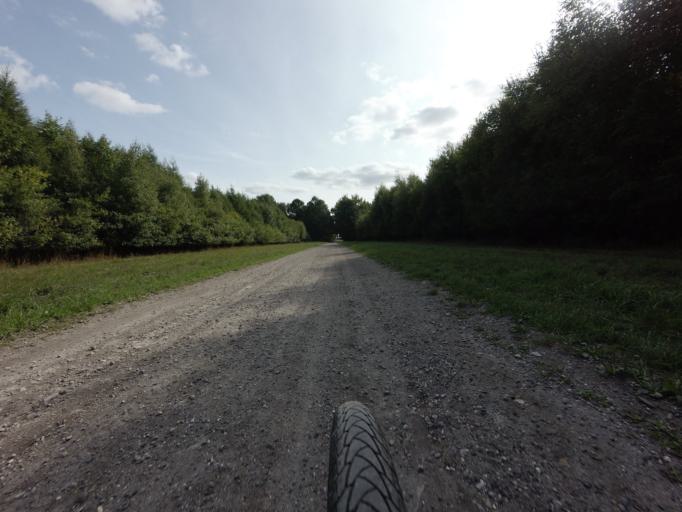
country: DK
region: Zealand
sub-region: Vordingborg Kommune
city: Praesto
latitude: 55.1536
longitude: 12.0945
